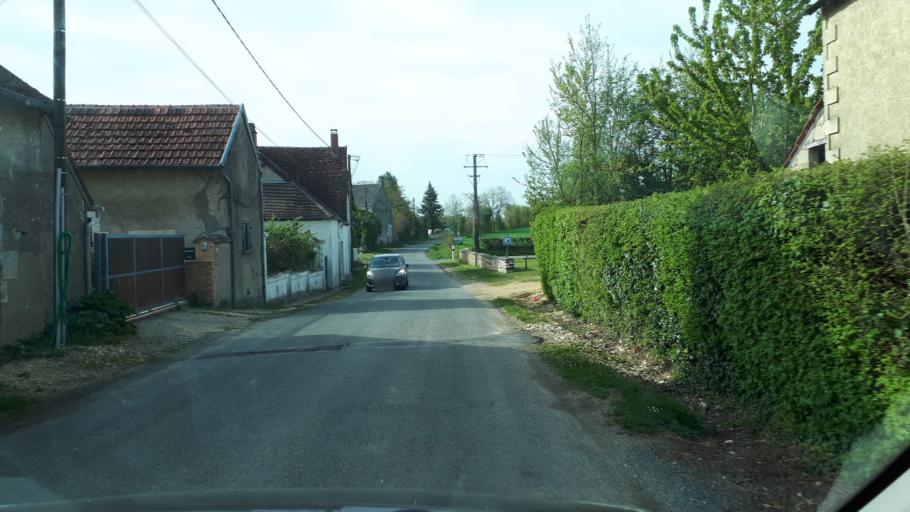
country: FR
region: Centre
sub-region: Departement du Cher
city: Sancerre
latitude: 47.2859
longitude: 2.7537
